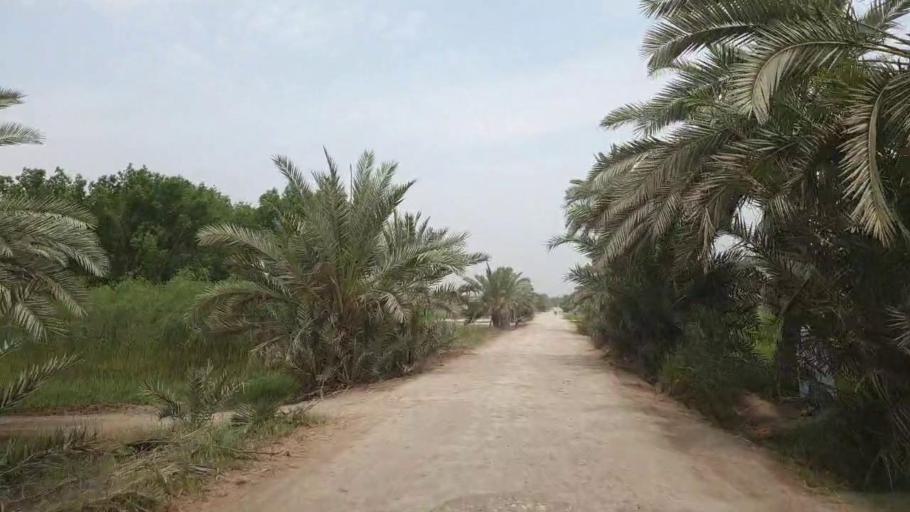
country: PK
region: Sindh
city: Pir jo Goth
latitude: 27.5183
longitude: 68.5803
